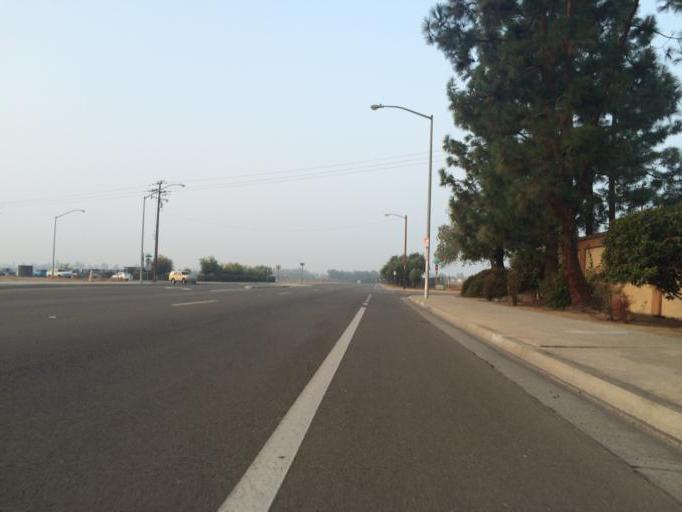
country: US
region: California
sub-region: Fresno County
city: Tarpey Village
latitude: 36.7898
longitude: -119.7311
